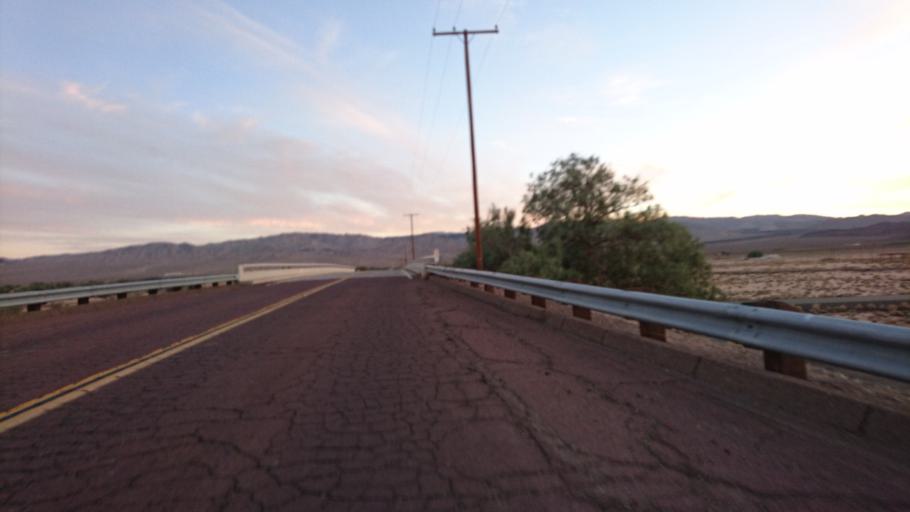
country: US
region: California
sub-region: San Bernardino County
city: Barstow
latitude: 34.8170
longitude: -116.6102
